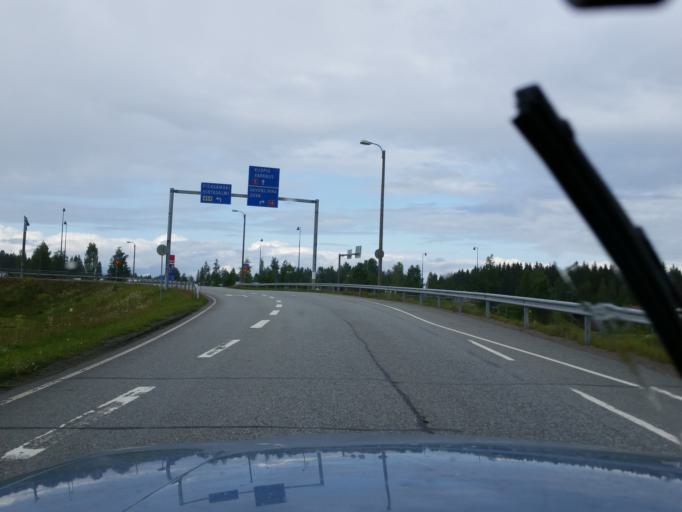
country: FI
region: Southern Savonia
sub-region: Pieksaemaeki
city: Juva
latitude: 61.8977
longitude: 27.8035
